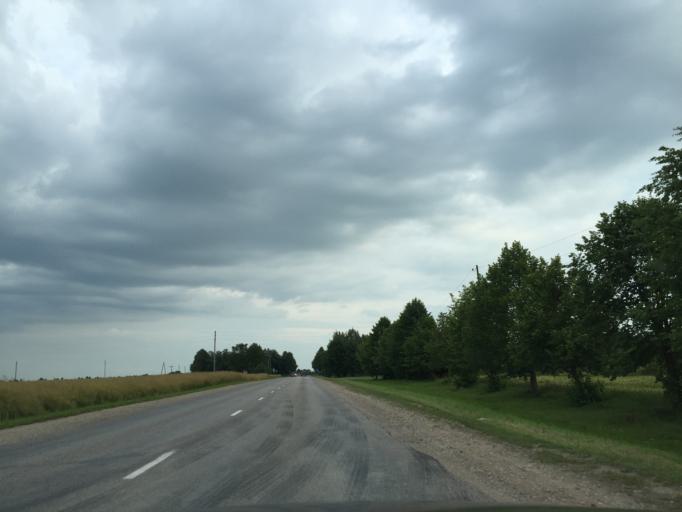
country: LV
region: Dobeles Rajons
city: Dobele
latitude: 56.5693
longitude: 23.2997
